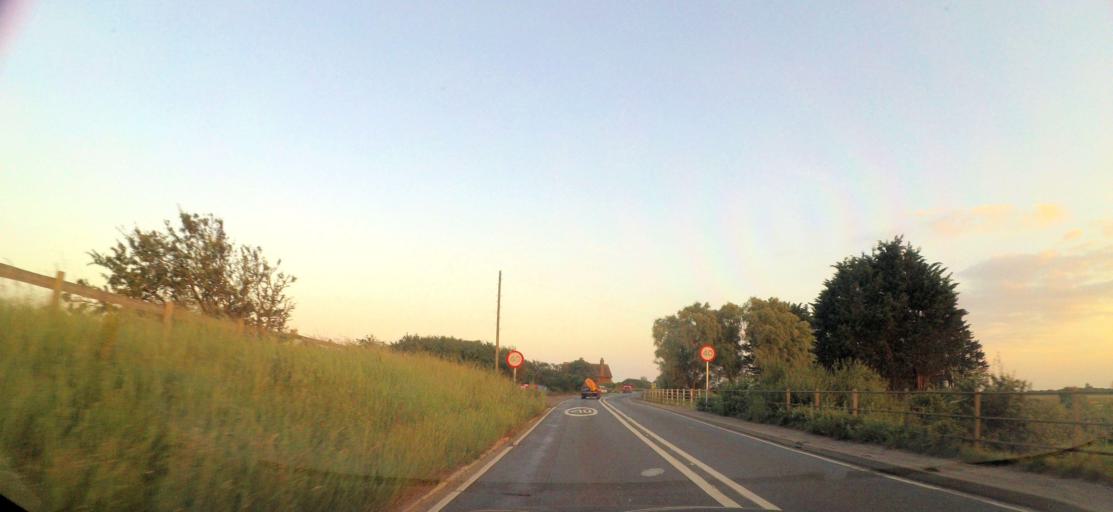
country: GB
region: England
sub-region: West Sussex
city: Selsey
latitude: 50.7603
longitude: -0.7872
